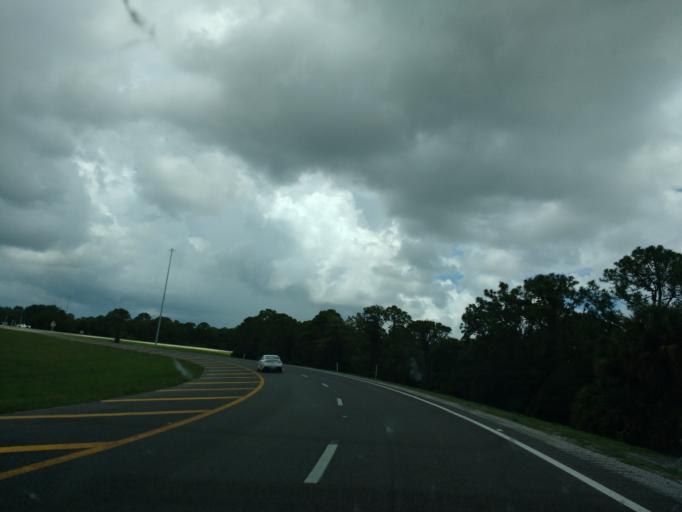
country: US
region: Florida
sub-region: Sarasota County
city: Plantation
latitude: 27.1127
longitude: -82.3821
